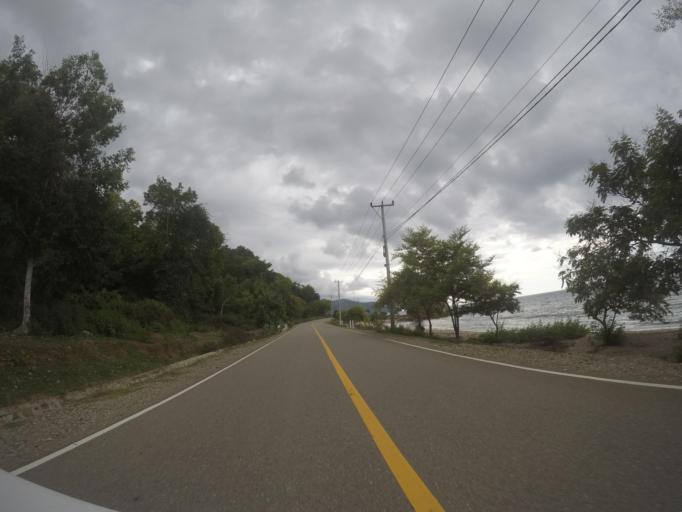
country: TL
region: Bobonaro
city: Maliana
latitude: -8.8103
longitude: 125.0854
